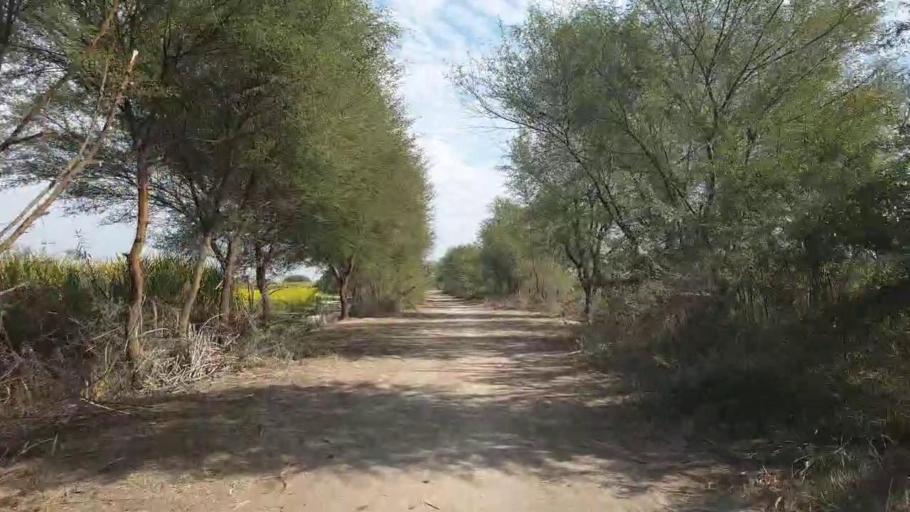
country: PK
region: Sindh
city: Jhol
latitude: 26.0101
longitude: 68.8774
